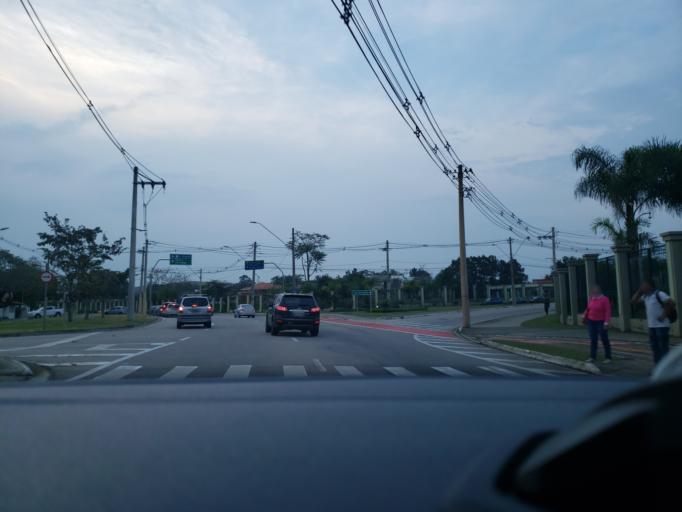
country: BR
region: Sao Paulo
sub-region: Sao Jose Dos Campos
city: Sao Jose dos Campos
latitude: -23.1931
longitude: -45.9217
